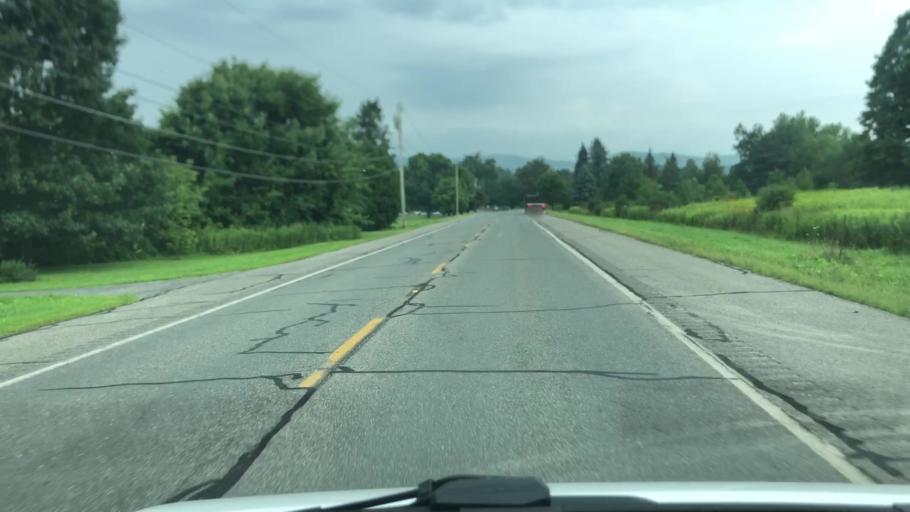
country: US
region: Massachusetts
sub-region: Berkshire County
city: Williamstown
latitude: 42.6532
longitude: -73.2382
